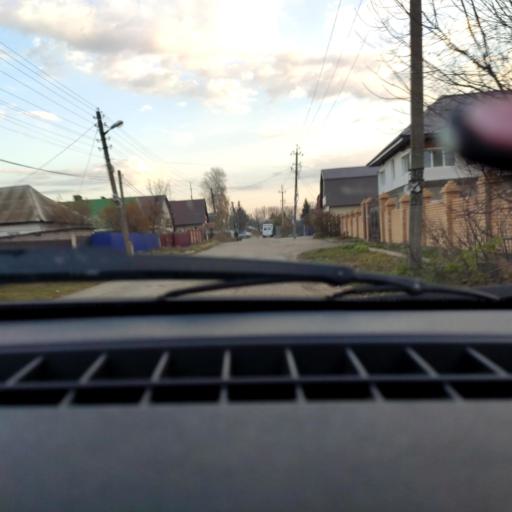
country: RU
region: Bashkortostan
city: Iglino
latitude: 54.8330
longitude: 56.1870
